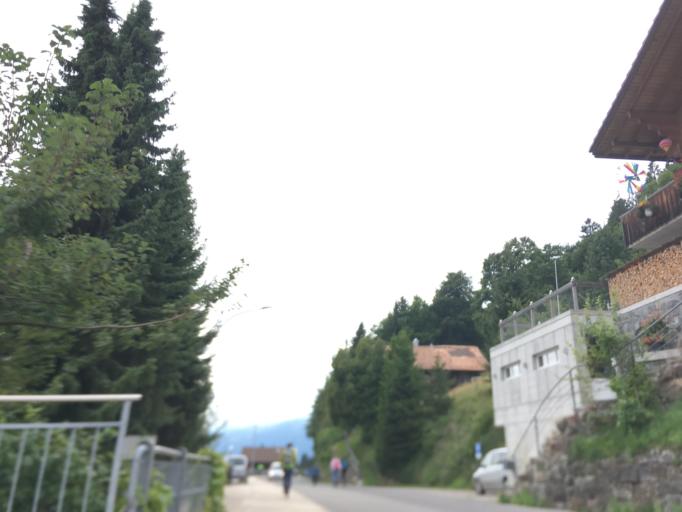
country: CH
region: Bern
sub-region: Interlaken-Oberhasli District
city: Beatenberg
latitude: 46.6916
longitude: 7.7842
